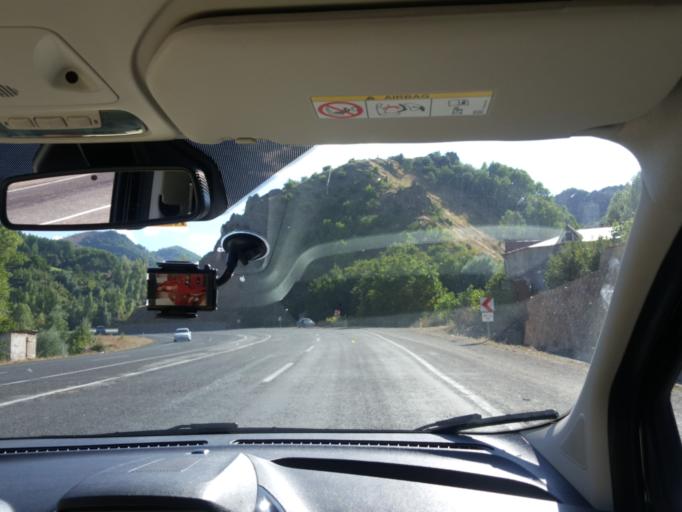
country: TR
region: Sivas
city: Aksu
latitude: 40.0475
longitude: 38.0453
